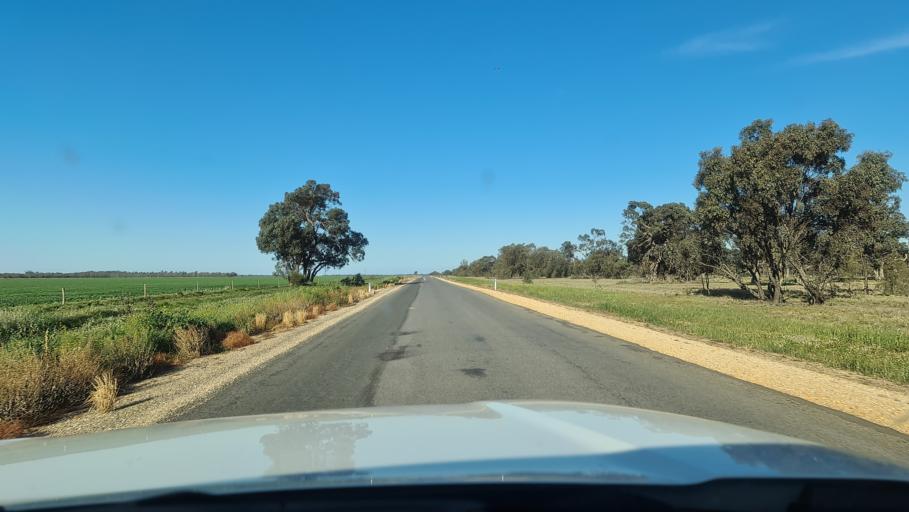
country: AU
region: Victoria
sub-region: Horsham
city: Horsham
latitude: -36.4492
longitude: 142.5423
